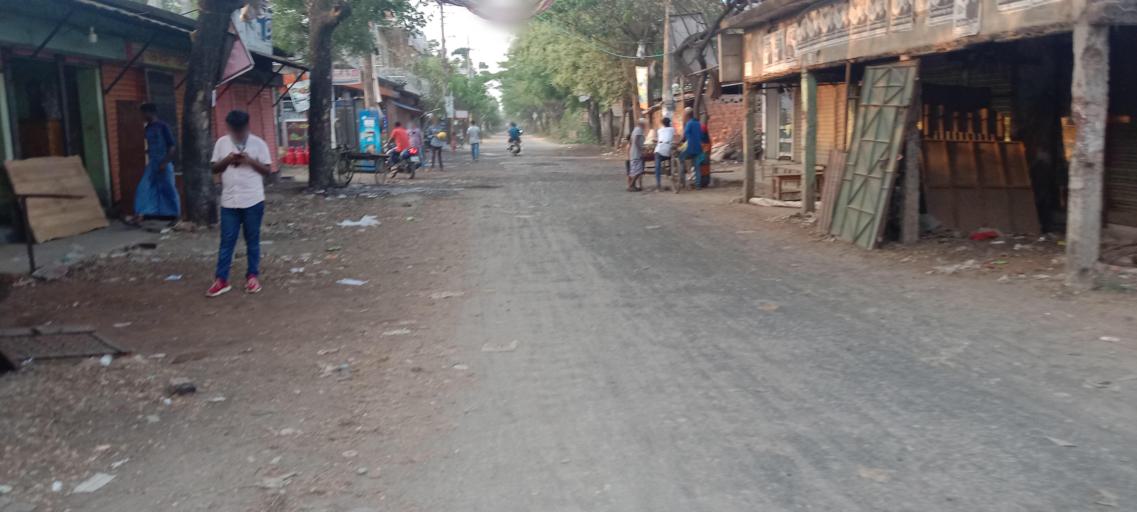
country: BD
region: Dhaka
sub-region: Dhaka
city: Dhaka
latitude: 23.6653
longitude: 90.4288
